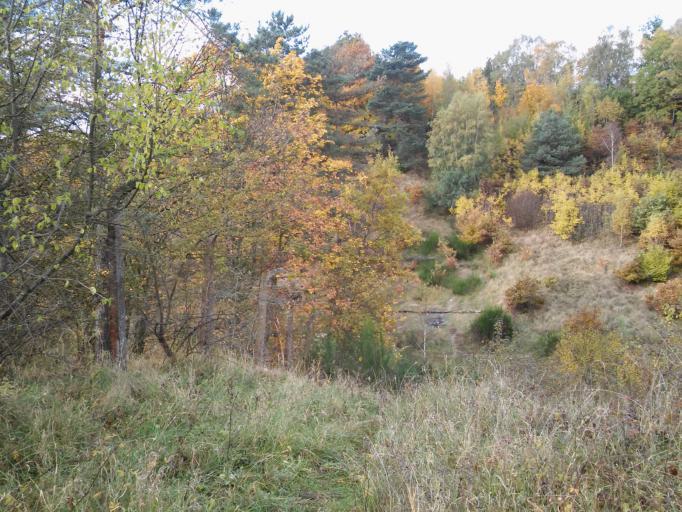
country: PL
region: Pomeranian Voivodeship
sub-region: Powiat gdanski
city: Kowale
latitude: 54.3676
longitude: 18.5835
